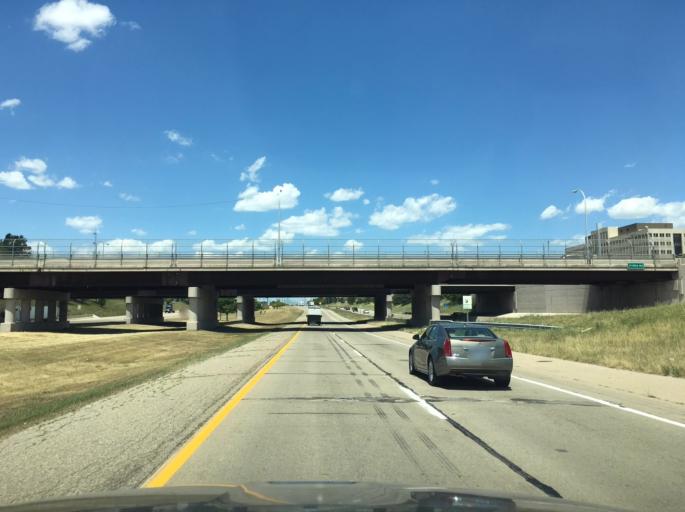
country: US
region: Michigan
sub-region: Macomb County
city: Center Line
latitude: 42.4906
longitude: -83.0455
